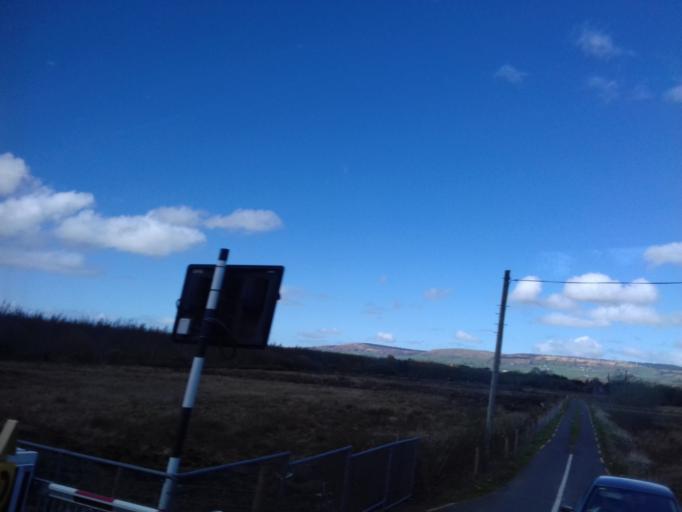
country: IE
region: Munster
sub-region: Ciarrai
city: Tralee
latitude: 52.2377
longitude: -9.5988
